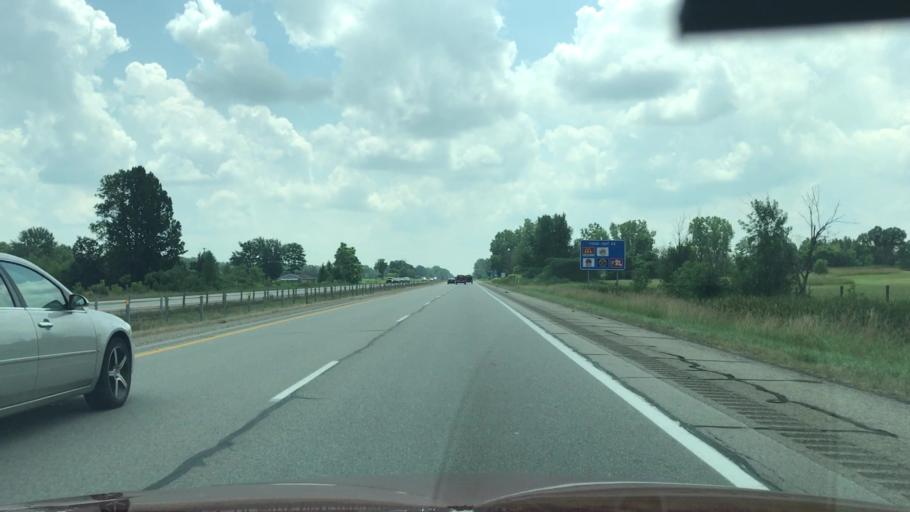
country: US
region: Michigan
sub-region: Allegan County
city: Wayland
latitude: 42.6988
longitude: -85.6598
